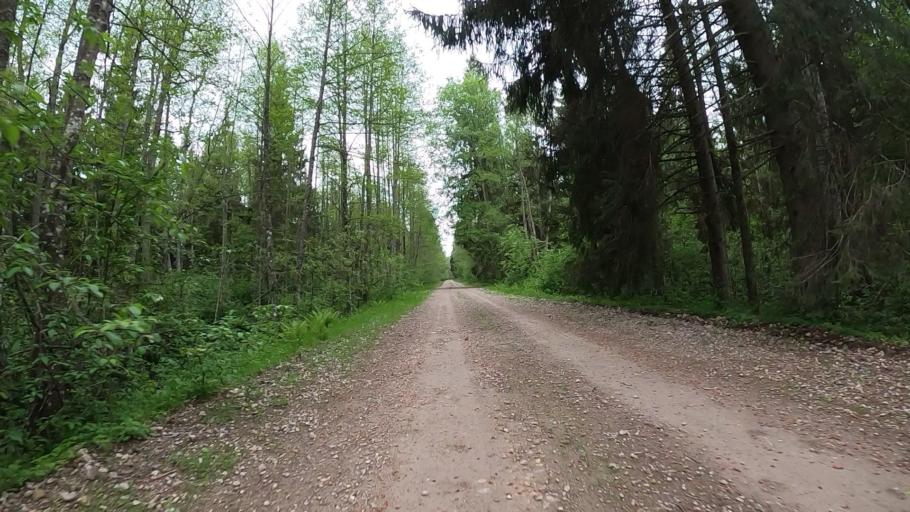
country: LV
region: Ozolnieku
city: Ozolnieki
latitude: 56.8040
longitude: 23.7851
